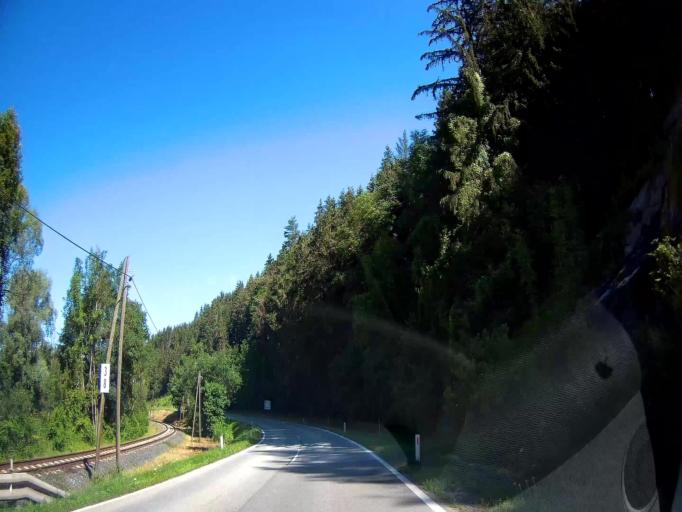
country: AT
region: Carinthia
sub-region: Politischer Bezirk Sankt Veit an der Glan
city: Bruckl
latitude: 46.7606
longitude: 14.4950
